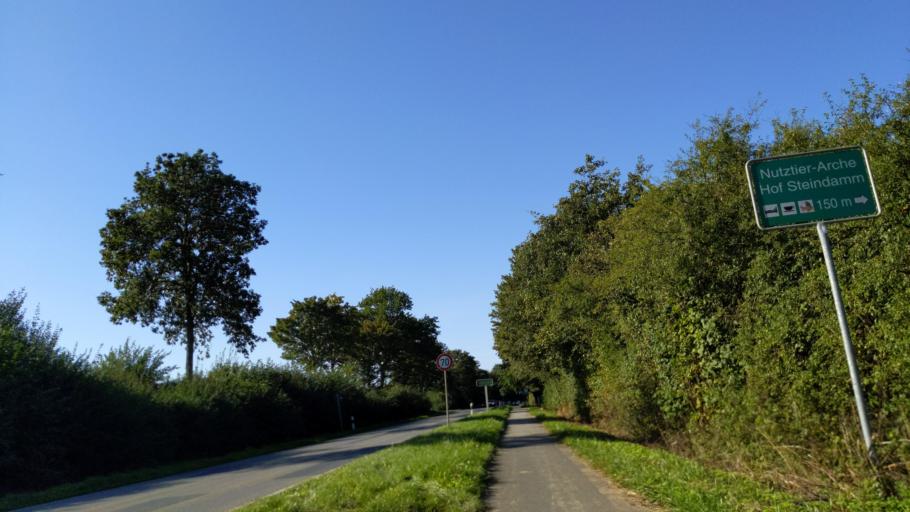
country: DE
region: Schleswig-Holstein
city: Ahrensbok
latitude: 53.9835
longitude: 10.5833
